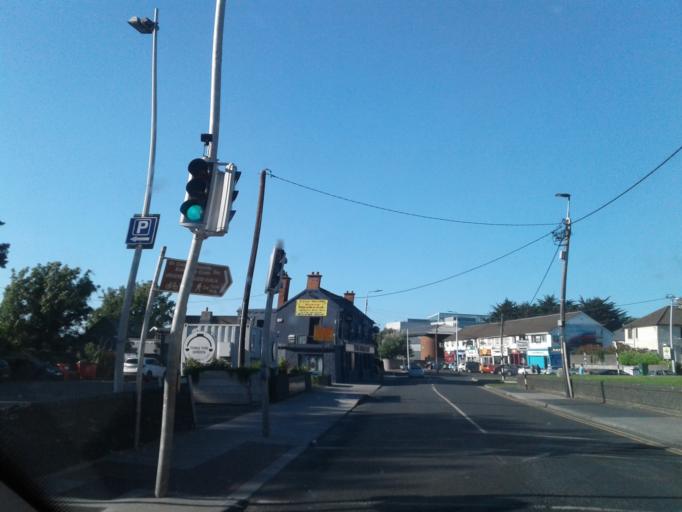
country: IE
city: Milltown
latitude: 53.3012
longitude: -6.2457
